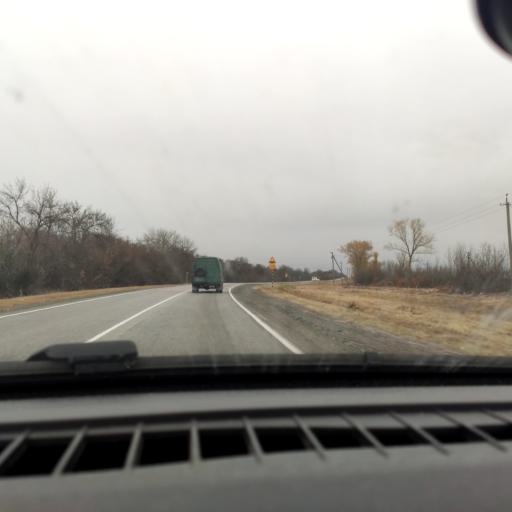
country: RU
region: Voronezj
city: Uryv-Pokrovka
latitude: 51.0757
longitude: 38.9956
